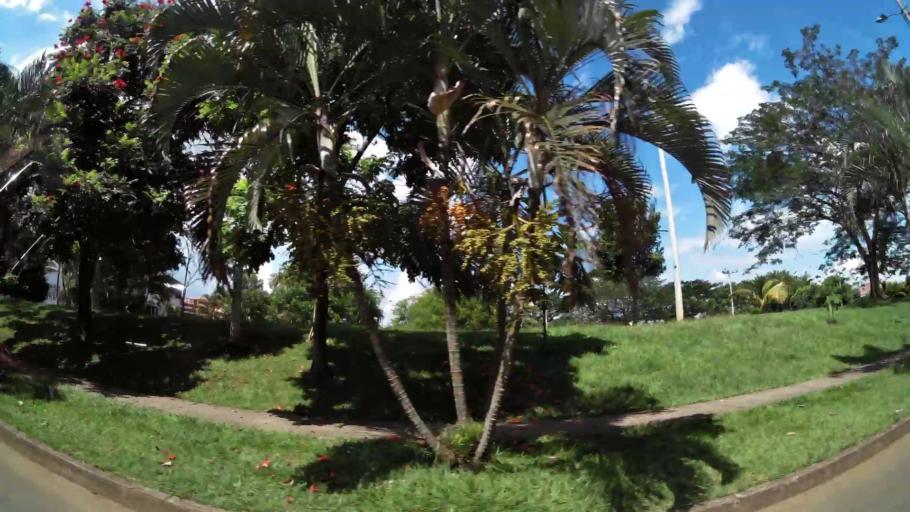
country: CO
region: Valle del Cauca
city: Cali
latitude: 3.3937
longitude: -76.5182
